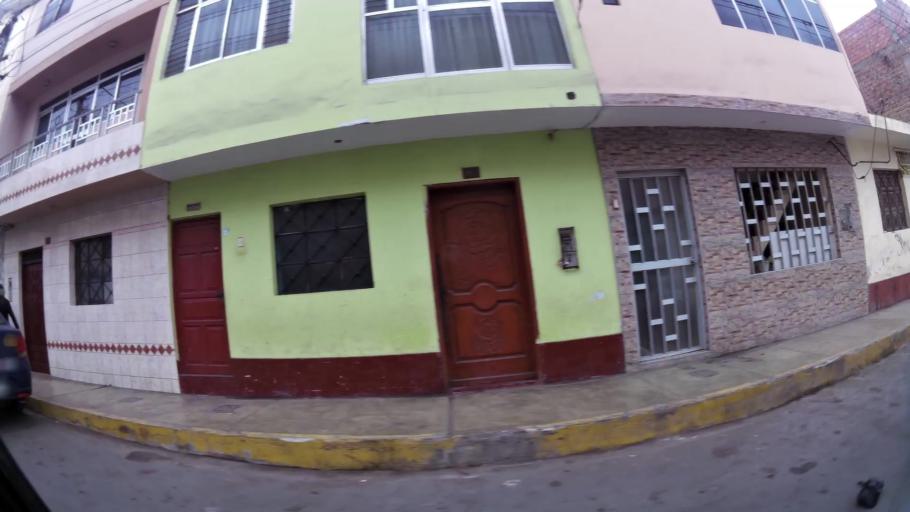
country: PE
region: Lima
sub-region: Barranca
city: Barranca
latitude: -10.7496
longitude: -77.7642
